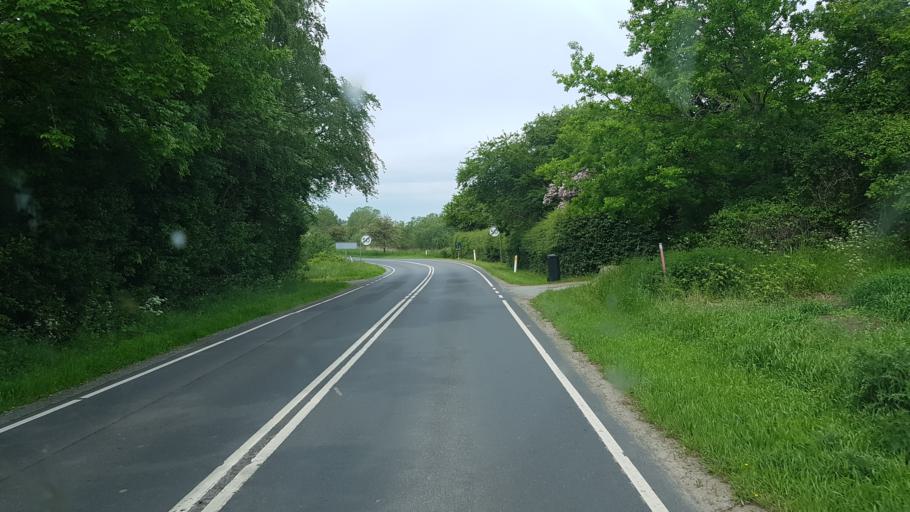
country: DK
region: South Denmark
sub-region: Nordfyns Kommune
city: Sonderso
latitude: 55.5713
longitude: 10.2060
